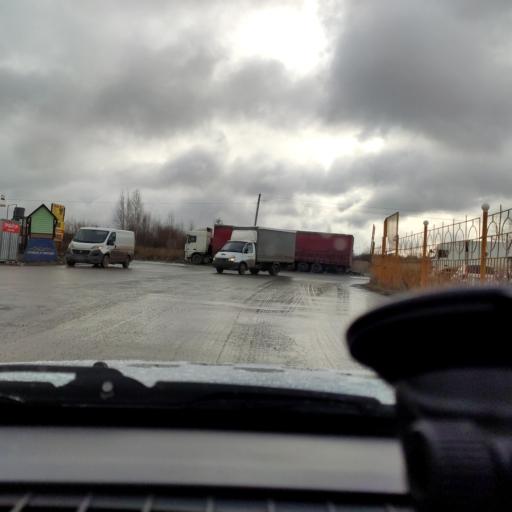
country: RU
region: Perm
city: Froly
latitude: 57.9569
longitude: 56.2776
